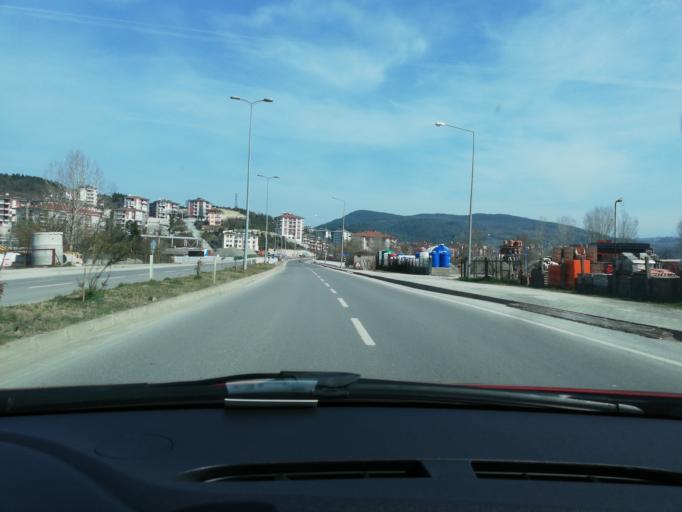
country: TR
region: Bartin
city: Bartin
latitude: 41.6402
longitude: 32.3547
